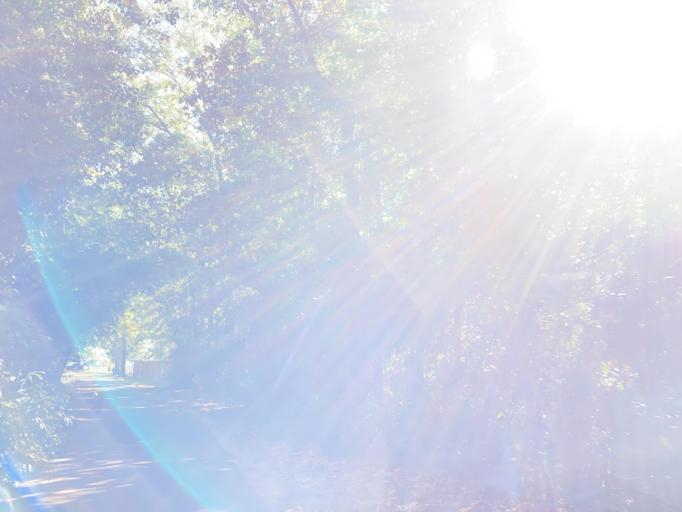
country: US
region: Mississippi
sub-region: Jackson County
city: Gulf Hills
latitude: 30.4183
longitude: -88.8424
